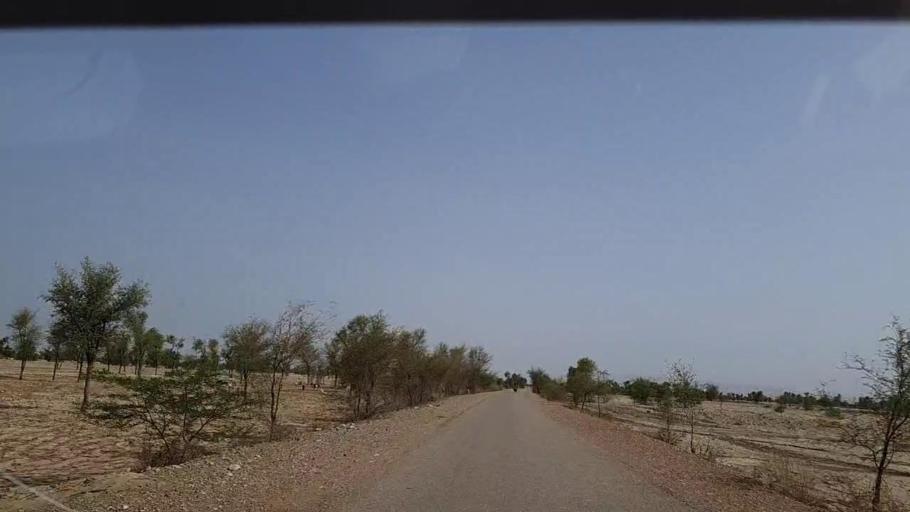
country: PK
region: Sindh
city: Johi
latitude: 26.6291
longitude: 67.5010
